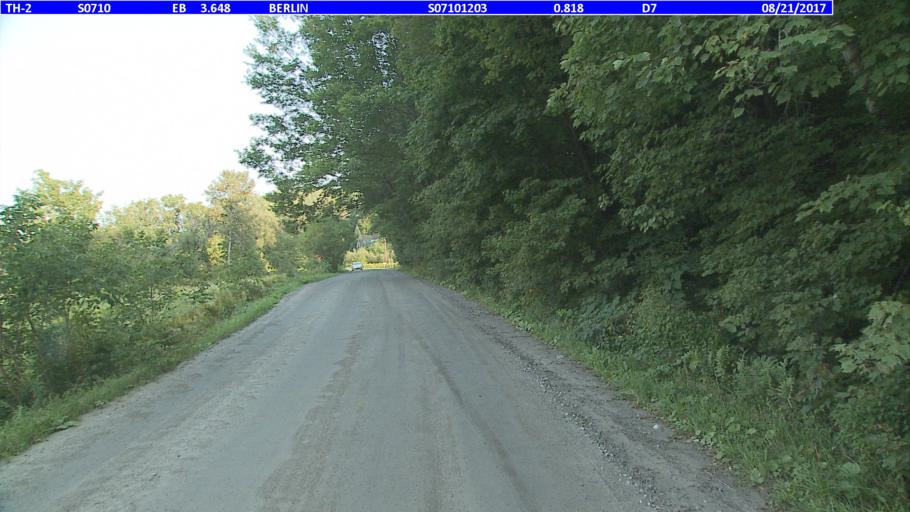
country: US
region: Vermont
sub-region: Washington County
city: Montpelier
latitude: 44.2635
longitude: -72.6267
